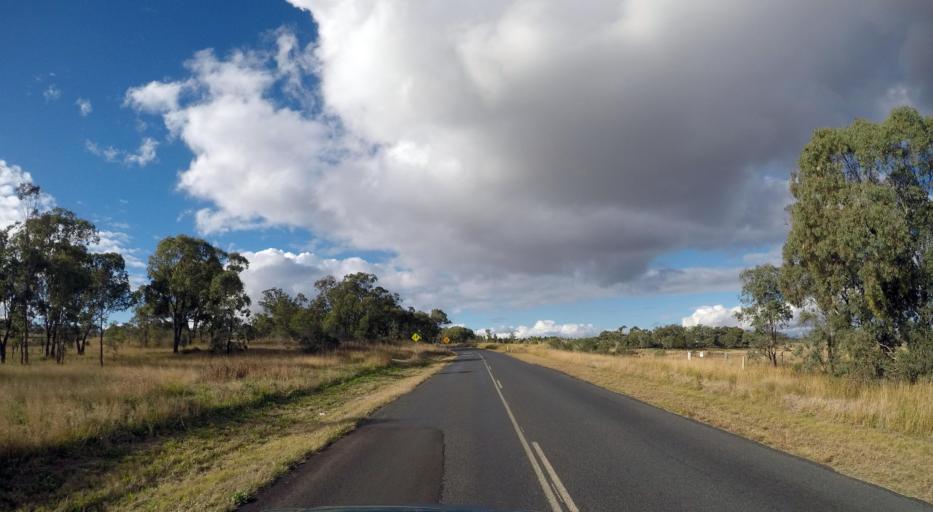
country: AU
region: Queensland
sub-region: Toowoomba
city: Westbrook
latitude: -27.7035
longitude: 151.6574
